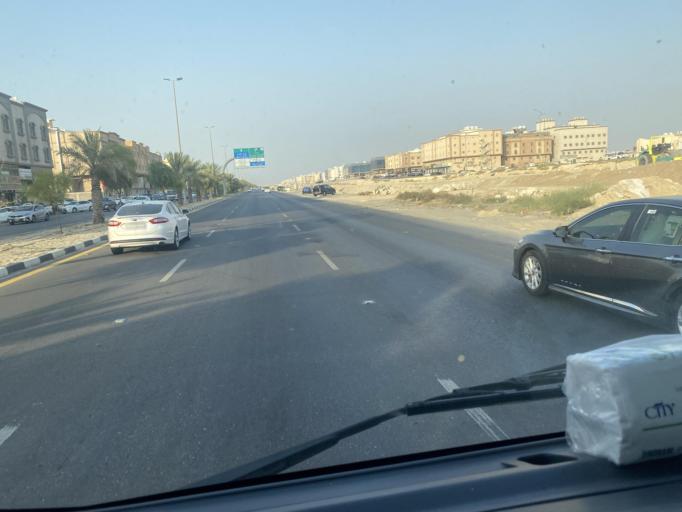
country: SA
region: Eastern Province
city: Dammam
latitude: 26.3618
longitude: 50.0692
